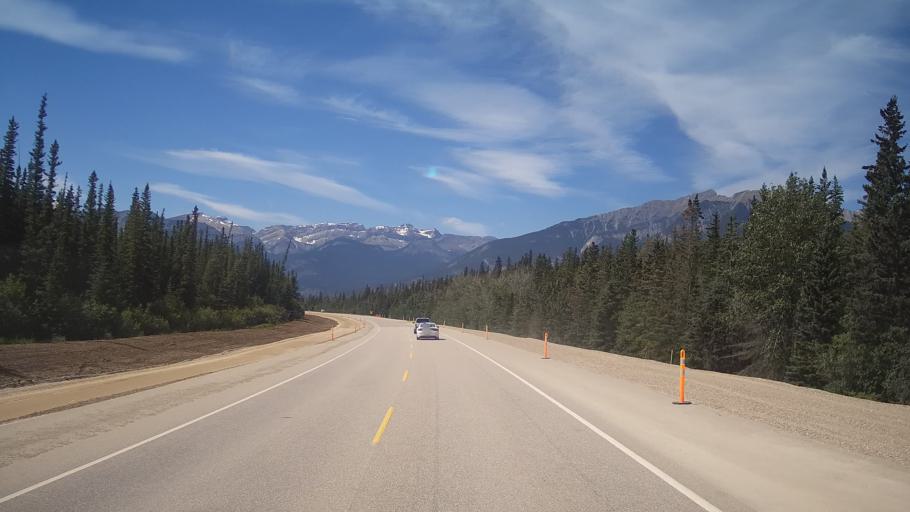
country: CA
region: Alberta
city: Jasper Park Lodge
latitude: 53.0697
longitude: -118.0566
